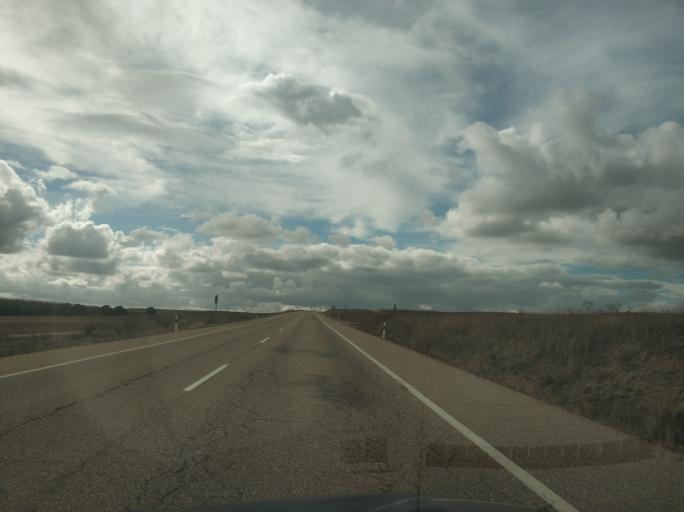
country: ES
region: Castille and Leon
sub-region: Provincia de Valladolid
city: Pollos
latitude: 41.4388
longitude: -5.0967
